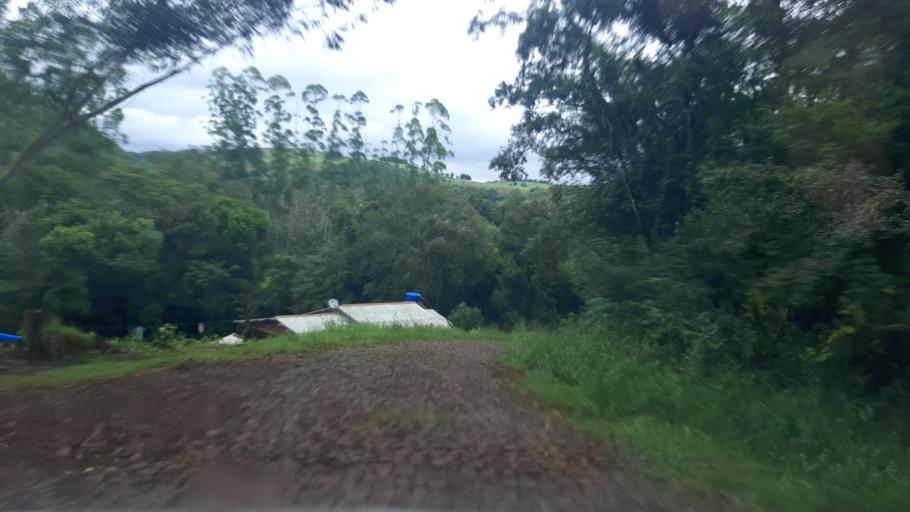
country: BR
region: Parana
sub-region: Ampere
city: Ampere
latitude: -26.0459
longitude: -53.5158
